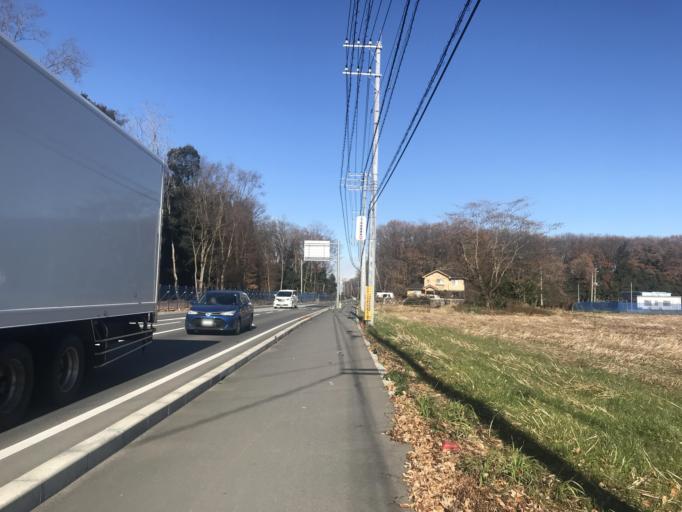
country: JP
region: Ibaraki
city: Yuki
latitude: 36.3412
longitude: 139.8788
